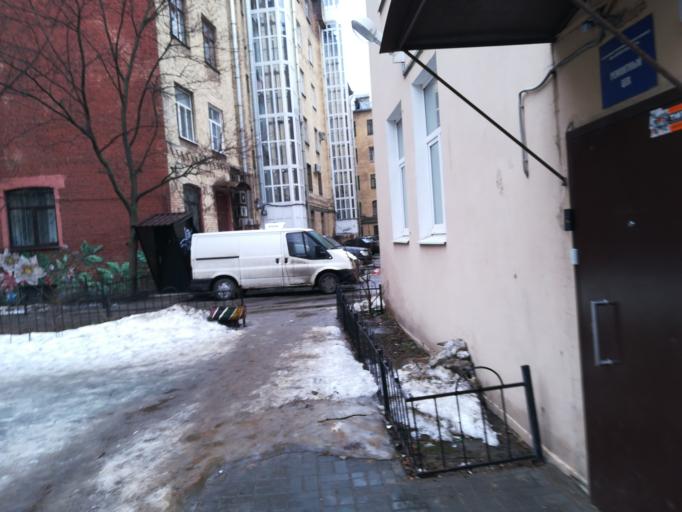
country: RU
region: St.-Petersburg
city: Petrogradka
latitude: 59.9576
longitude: 30.3309
